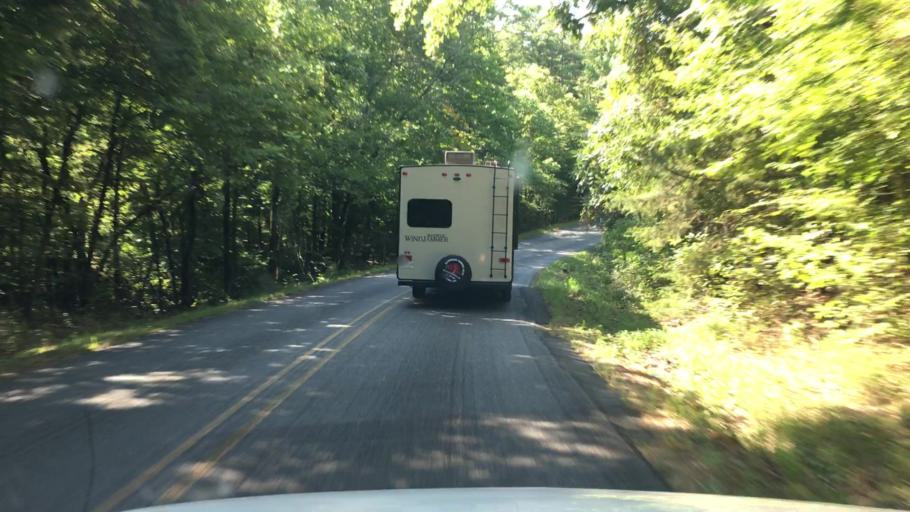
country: US
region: Arkansas
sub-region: Garland County
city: Piney
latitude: 34.5351
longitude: -93.3395
